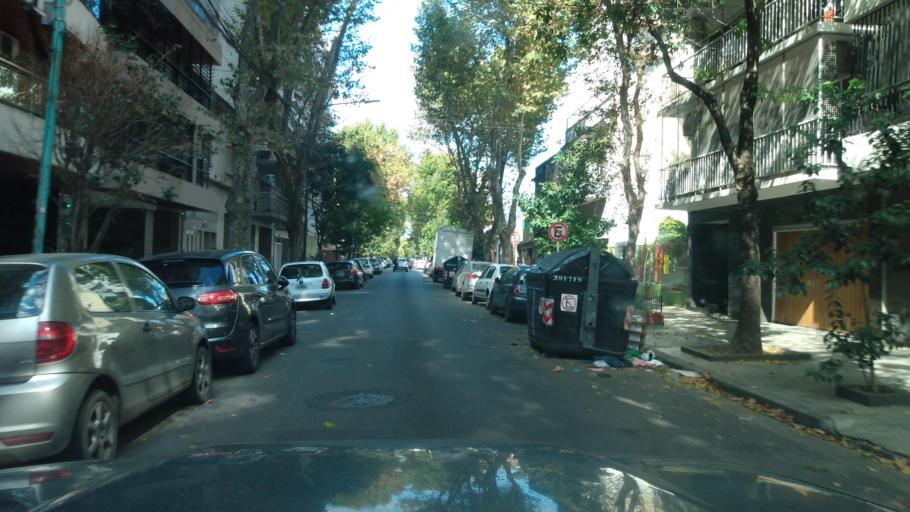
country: AR
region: Buenos Aires F.D.
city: Villa Santa Rita
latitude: -34.5793
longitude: -58.4890
